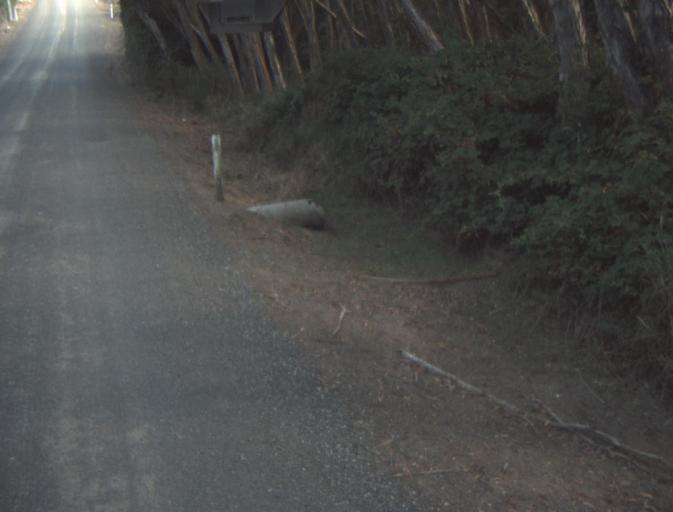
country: AU
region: Tasmania
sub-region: Launceston
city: Mayfield
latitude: -41.2742
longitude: 147.1845
